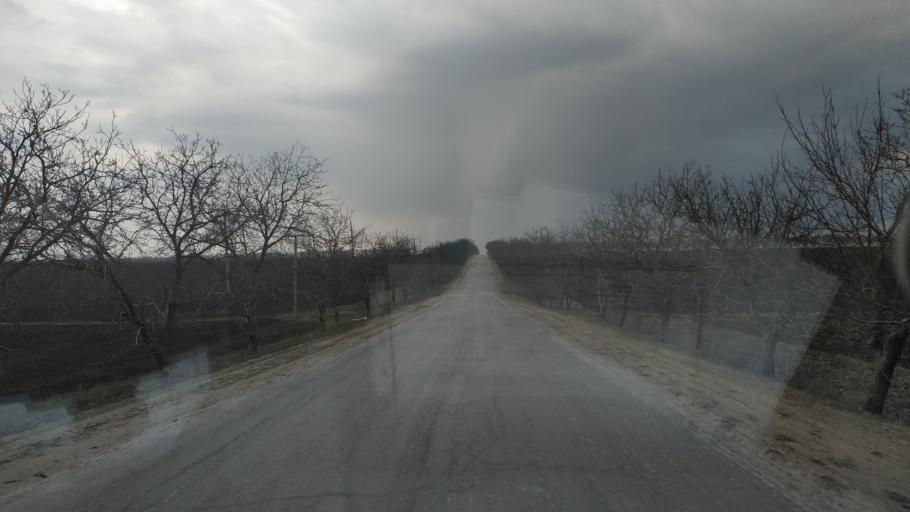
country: MD
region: Telenesti
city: Grigoriopol
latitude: 47.0253
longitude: 29.2910
